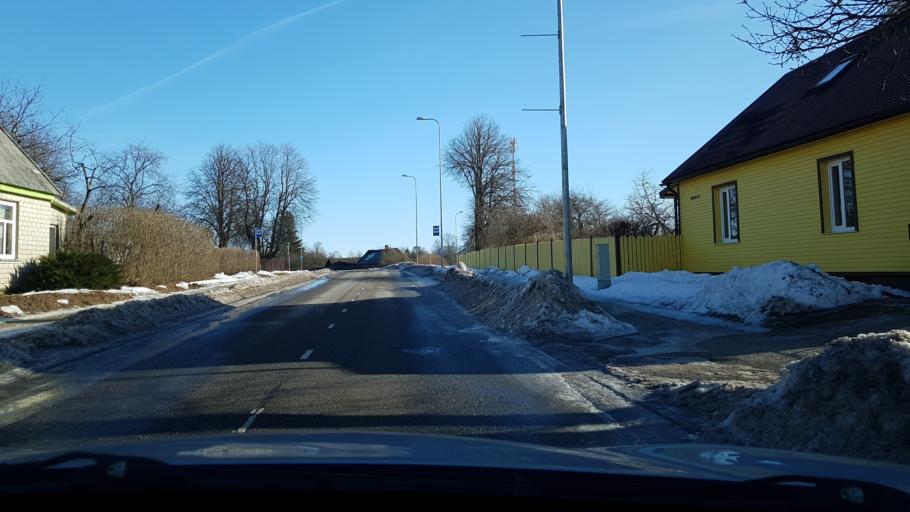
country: EE
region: Viljandimaa
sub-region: Suure-Jaani vald
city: Suure-Jaani
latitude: 58.5362
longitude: 25.4792
